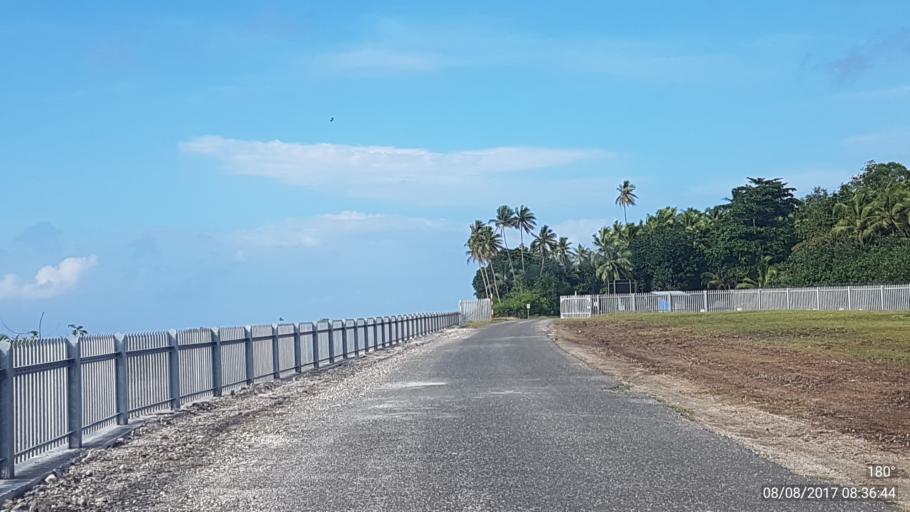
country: PG
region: Manus
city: Lorengau
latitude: -2.0733
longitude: 147.4282
